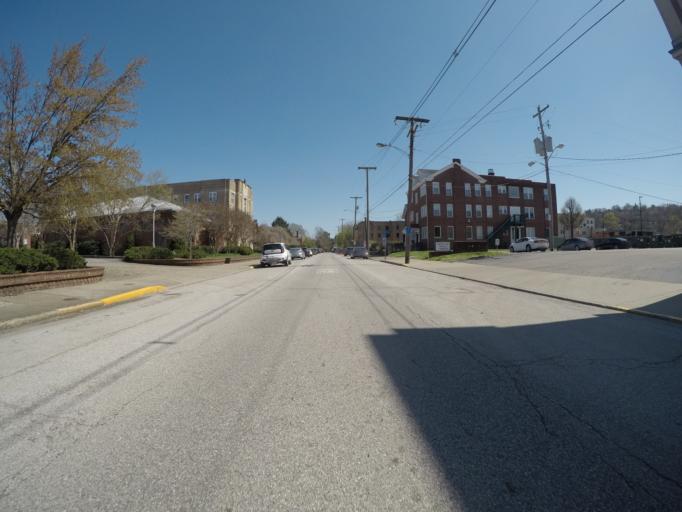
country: US
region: West Virginia
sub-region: Kanawha County
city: Charleston
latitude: 38.3436
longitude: -81.6290
